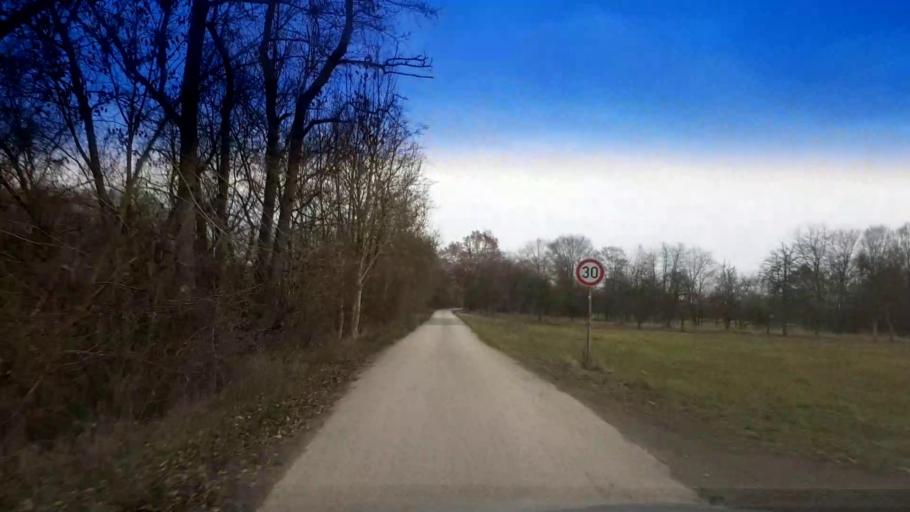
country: DE
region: Bavaria
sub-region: Upper Franconia
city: Kemmern
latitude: 49.9541
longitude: 10.8648
